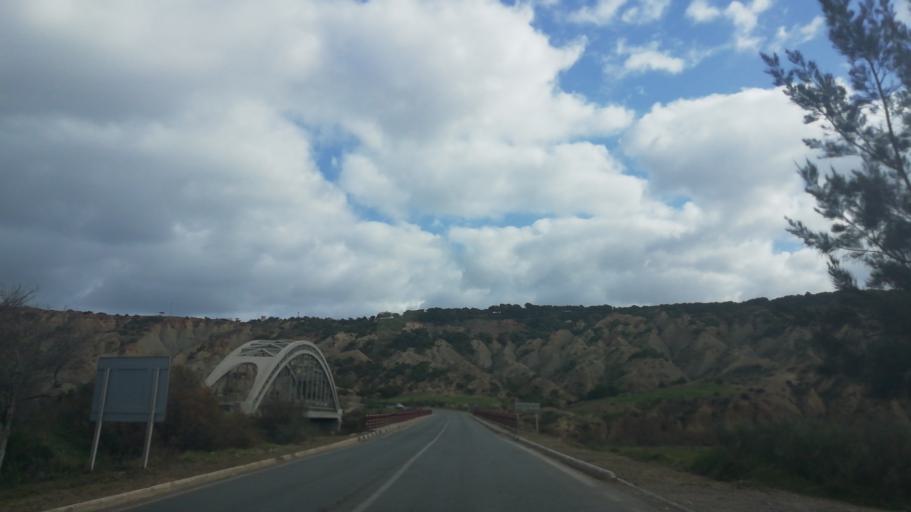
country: DZ
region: Relizane
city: Mazouna
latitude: 36.3031
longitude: 0.6693
